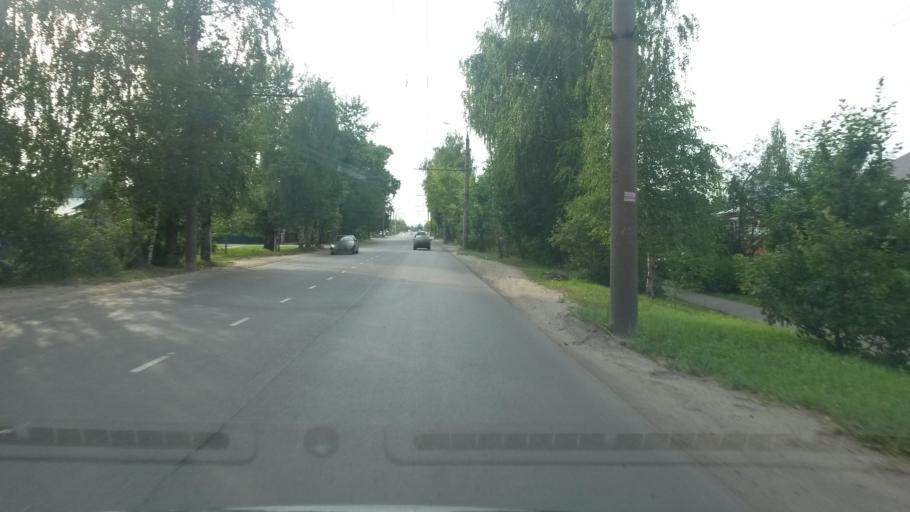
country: RU
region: Ivanovo
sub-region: Gorod Ivanovo
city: Ivanovo
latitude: 57.0142
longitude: 40.9326
